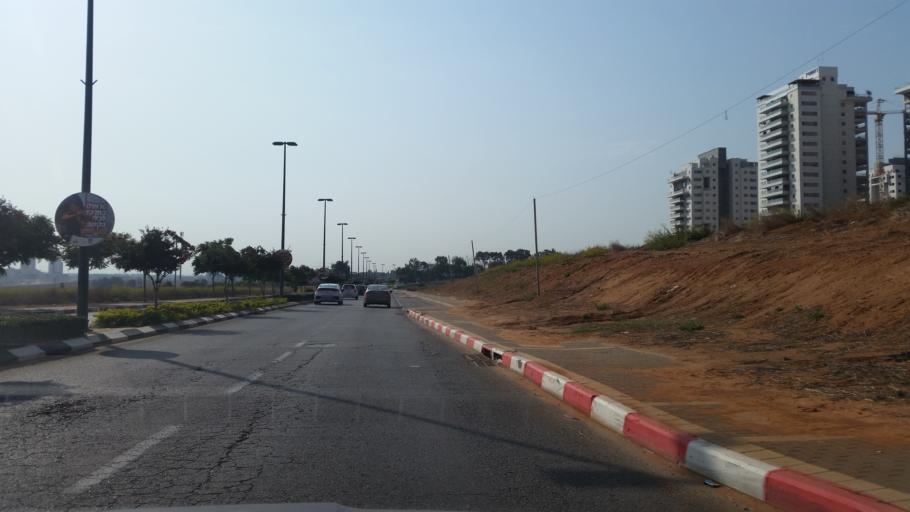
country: IL
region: Central District
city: Netanya
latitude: 32.3119
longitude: 34.8613
